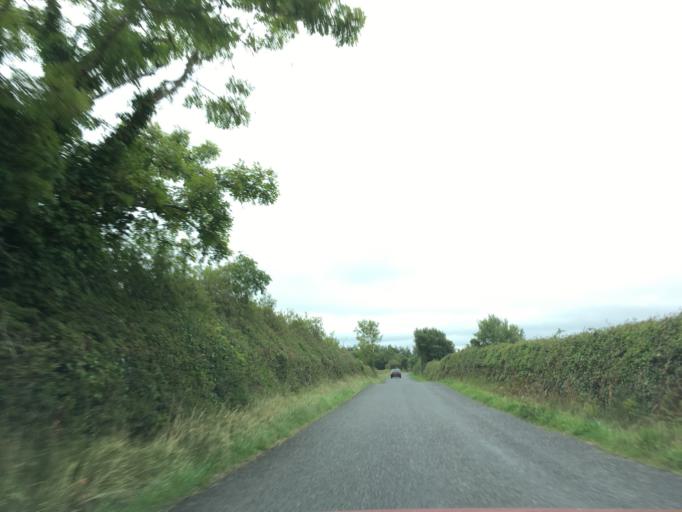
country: IE
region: Munster
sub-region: An Clar
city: Ennis
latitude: 52.7188
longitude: -9.0753
